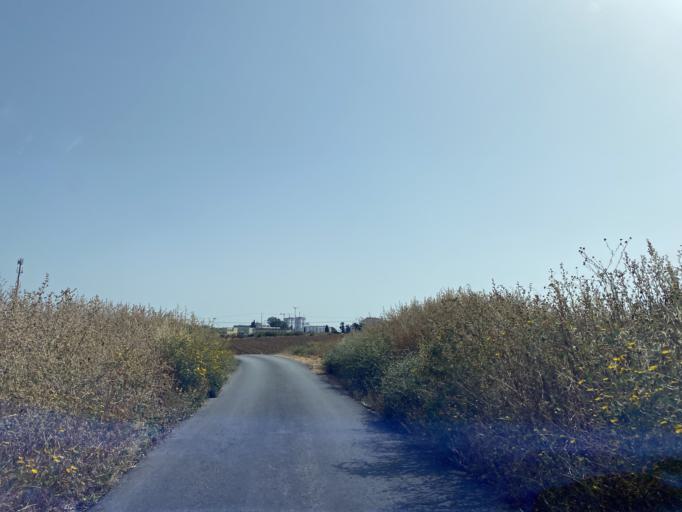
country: IL
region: Central District
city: Netanya
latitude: 32.3060
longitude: 34.8620
